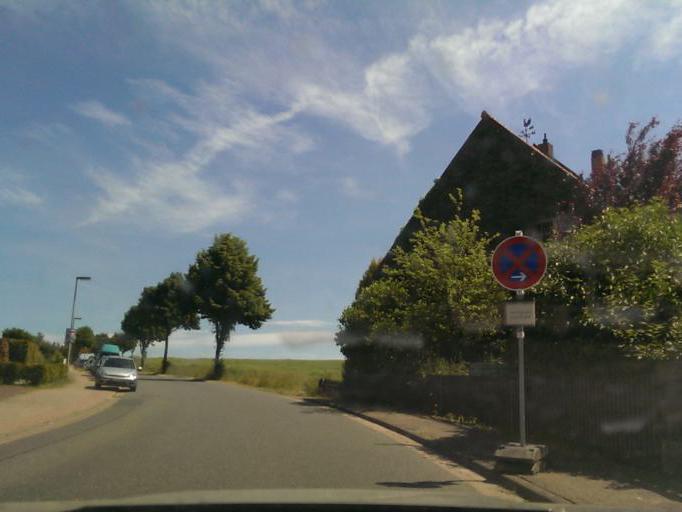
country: DE
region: Lower Saxony
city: Coppengrave
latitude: 51.9864
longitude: 9.7684
